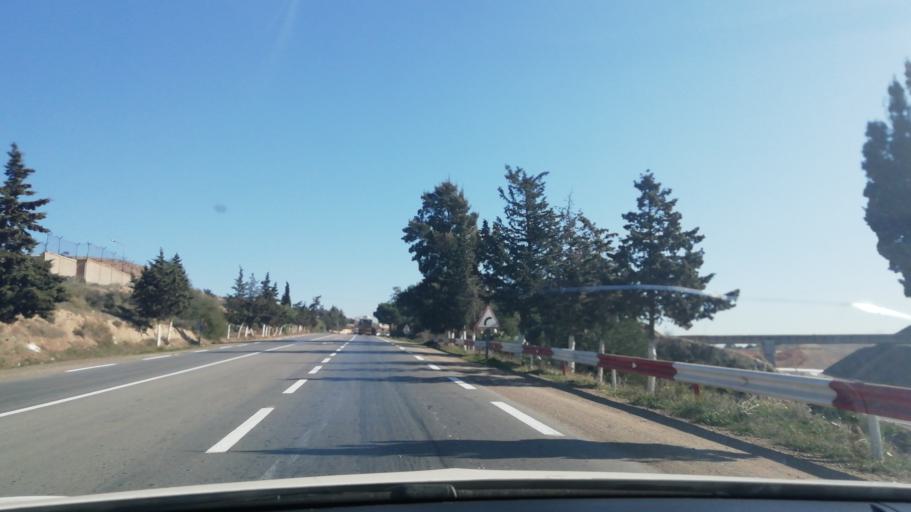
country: DZ
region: Tlemcen
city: Nedroma
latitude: 35.0880
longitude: -1.8148
